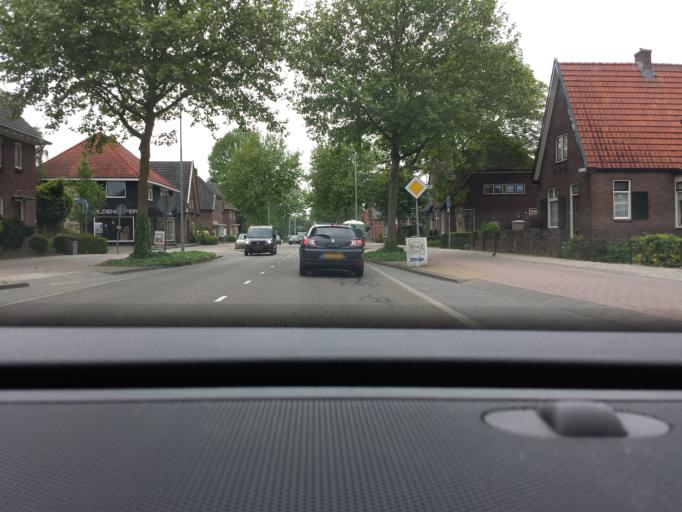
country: NL
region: Gelderland
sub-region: Gemeente Doetinchem
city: Doetinchem
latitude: 51.9666
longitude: 6.3059
